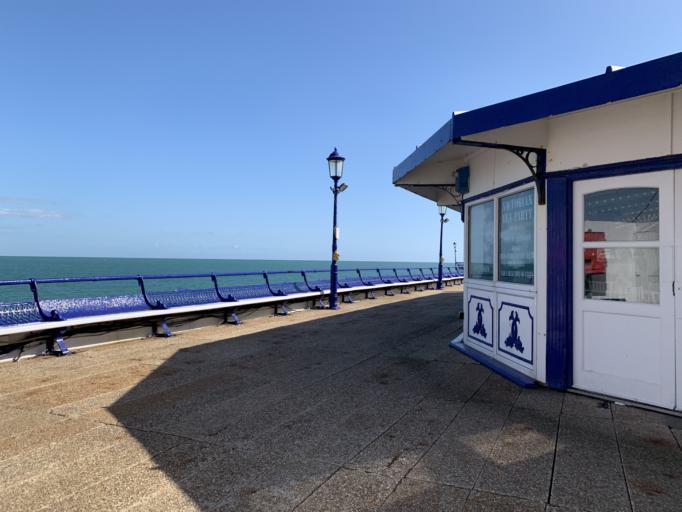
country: GB
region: England
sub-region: East Sussex
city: Eastbourne
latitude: 50.7664
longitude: 0.2943
